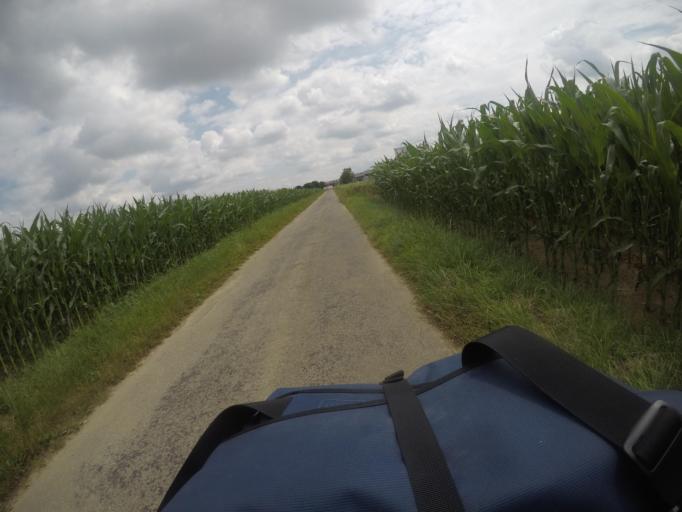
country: DE
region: Bavaria
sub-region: Swabia
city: Memmingen
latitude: 48.0064
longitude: 10.1670
